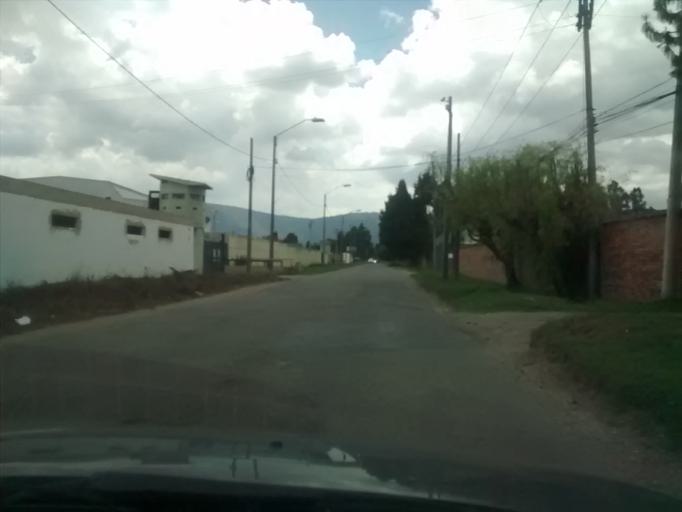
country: CO
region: Cundinamarca
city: Cota
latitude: 4.8145
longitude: -74.0612
